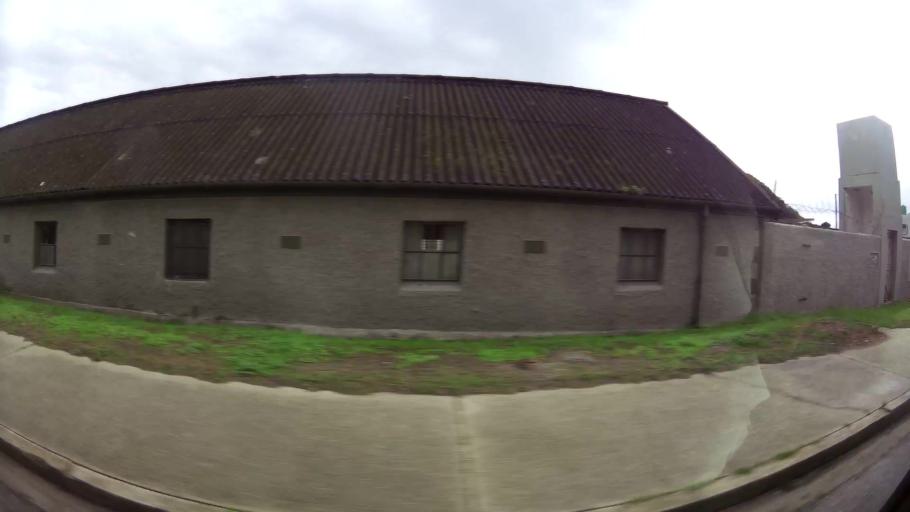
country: ZA
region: Eastern Cape
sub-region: Nelson Mandela Bay Metropolitan Municipality
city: Port Elizabeth
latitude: -33.9689
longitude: 25.6206
